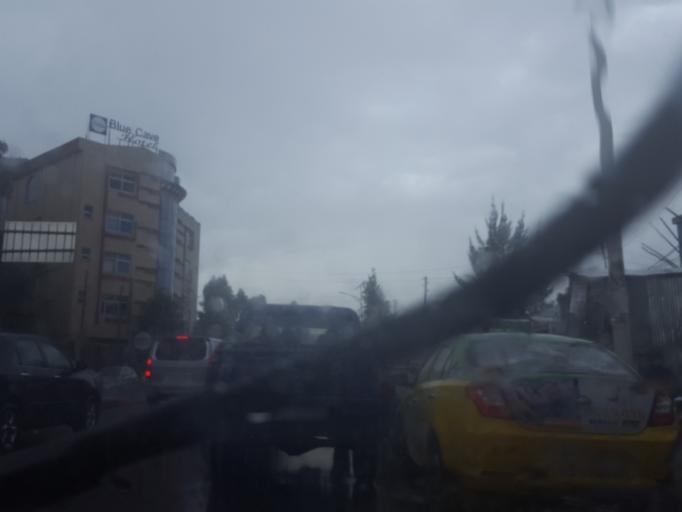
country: ET
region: Adis Abeba
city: Addis Ababa
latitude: 9.0166
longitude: 38.7820
